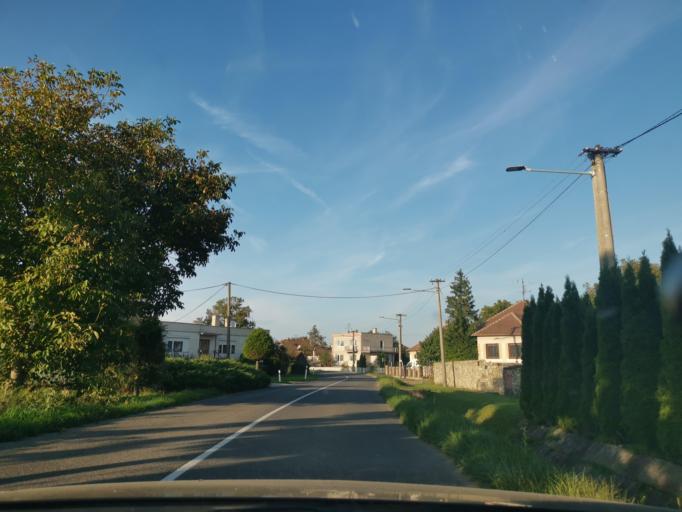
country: SK
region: Trnavsky
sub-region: Okres Senica
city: Senica
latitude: 48.6742
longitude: 17.2569
